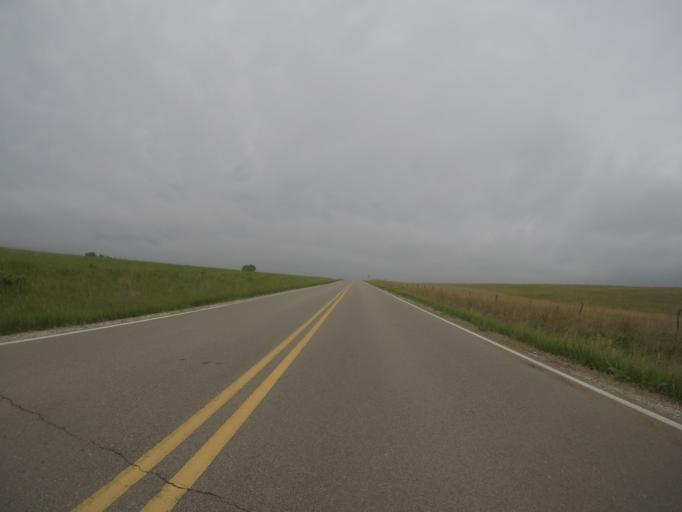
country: US
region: Kansas
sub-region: Pottawatomie County
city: Westmoreland
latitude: 39.5147
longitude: -96.2395
